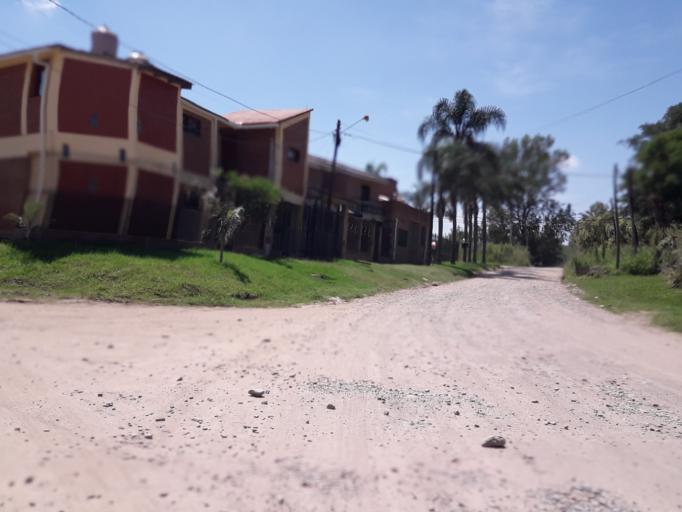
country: AR
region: Jujuy
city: San Salvador de Jujuy
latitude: -24.1809
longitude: -65.3366
